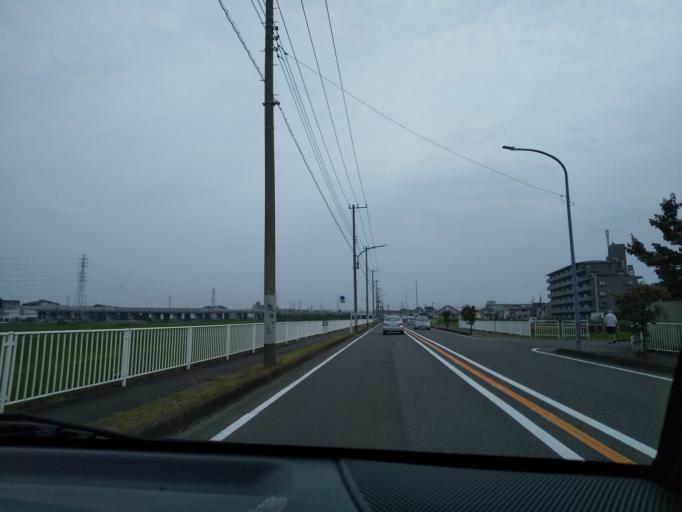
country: JP
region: Kanagawa
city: Atsugi
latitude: 35.4298
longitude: 139.3904
